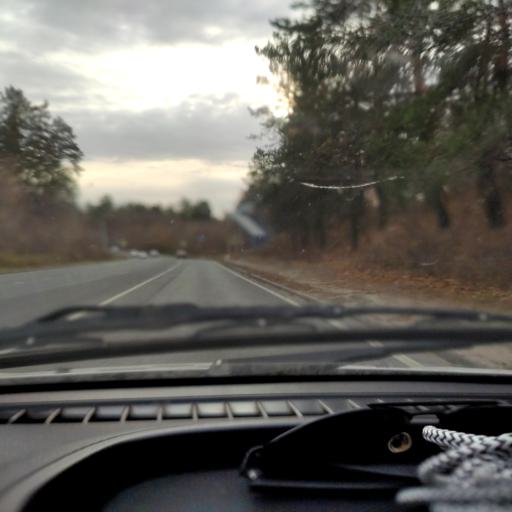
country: RU
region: Samara
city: Tol'yatti
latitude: 53.4947
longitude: 49.2904
